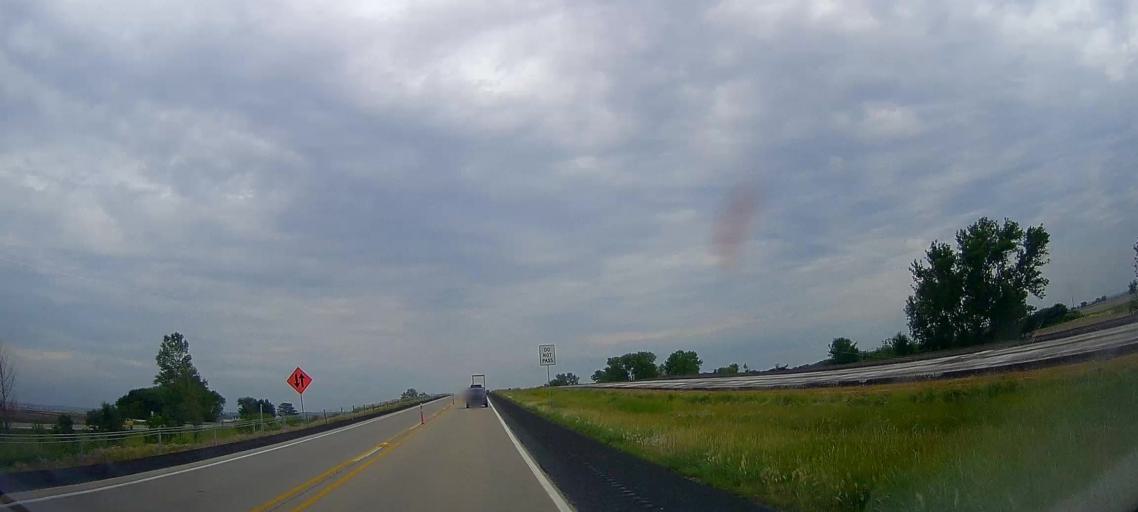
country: US
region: Nebraska
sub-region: Washington County
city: Blair
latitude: 41.6420
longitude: -96.0160
